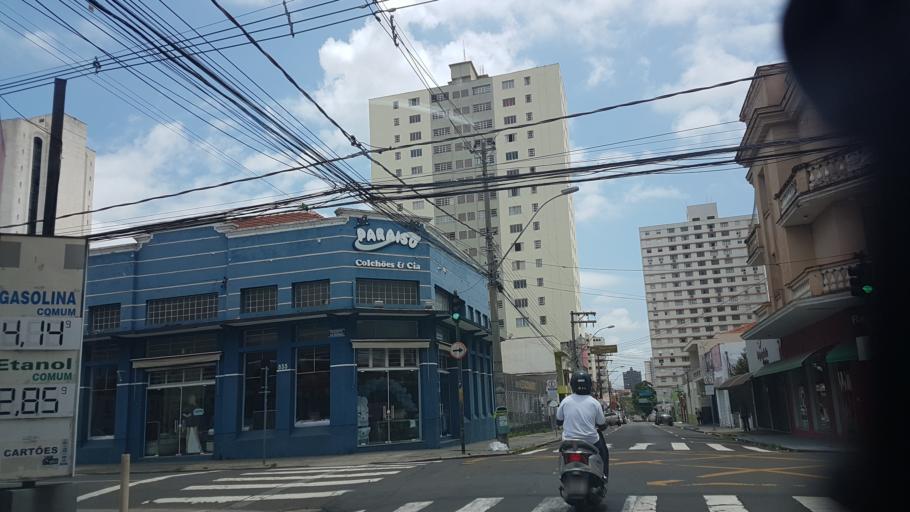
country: BR
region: Sao Paulo
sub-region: Piracicaba
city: Piracicaba
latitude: -22.7243
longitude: -47.6471
